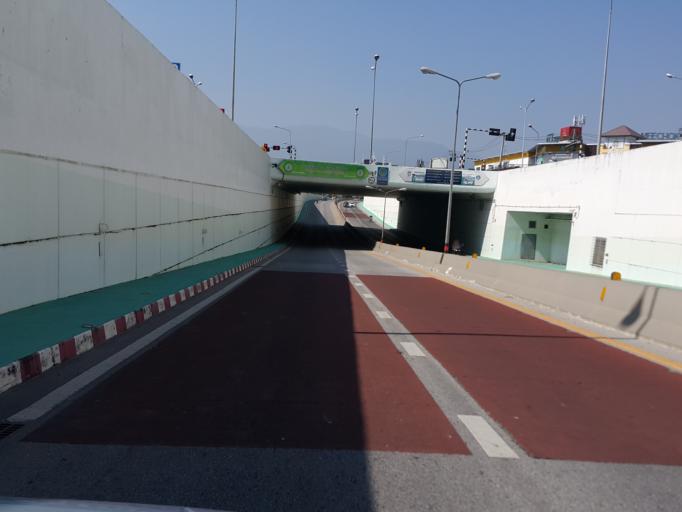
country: TH
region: Chiang Mai
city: San Sai
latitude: 18.8230
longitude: 99.0129
